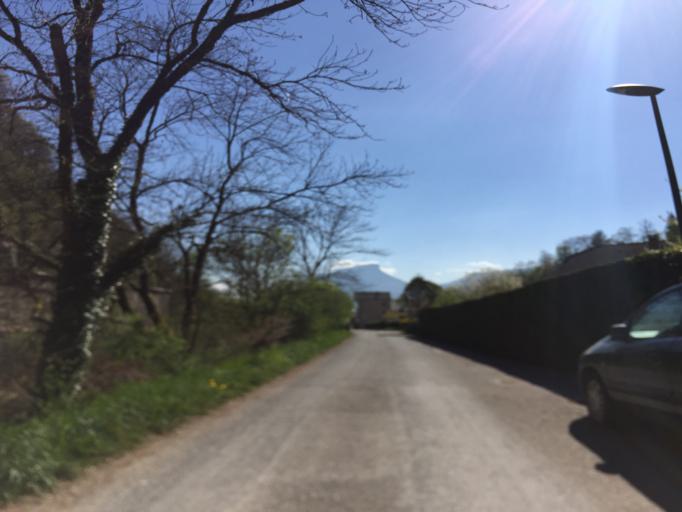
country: FR
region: Rhone-Alpes
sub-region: Departement de la Savoie
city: Barby
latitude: 45.5800
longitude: 5.9753
